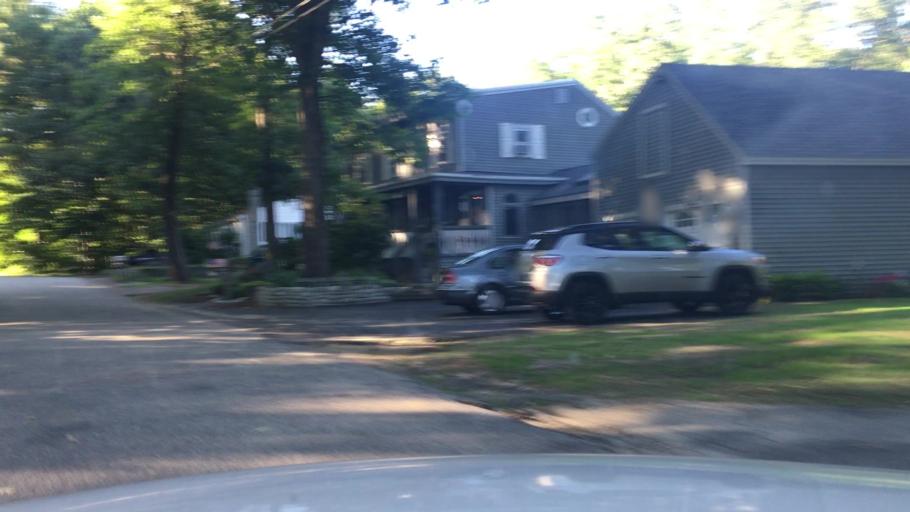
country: US
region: New Hampshire
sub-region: Rockingham County
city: Danville
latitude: 42.9023
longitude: -71.1510
